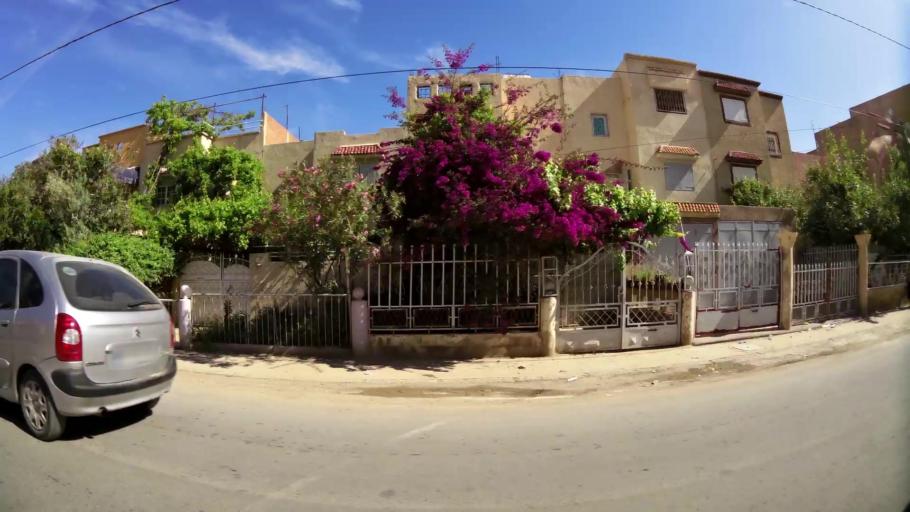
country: MA
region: Oriental
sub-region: Oujda-Angad
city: Oujda
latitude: 34.6574
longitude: -1.9380
